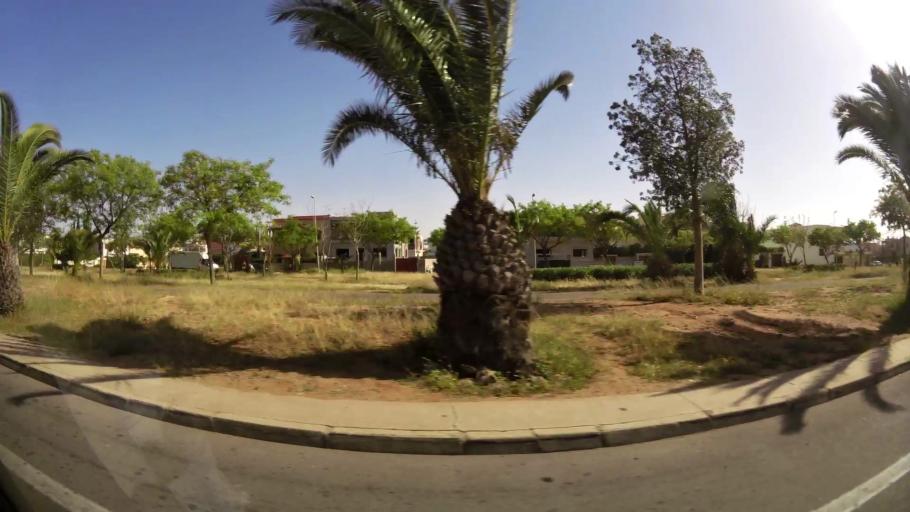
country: MA
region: Oued ed Dahab-Lagouira
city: Dakhla
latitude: 30.4044
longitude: -9.5373
